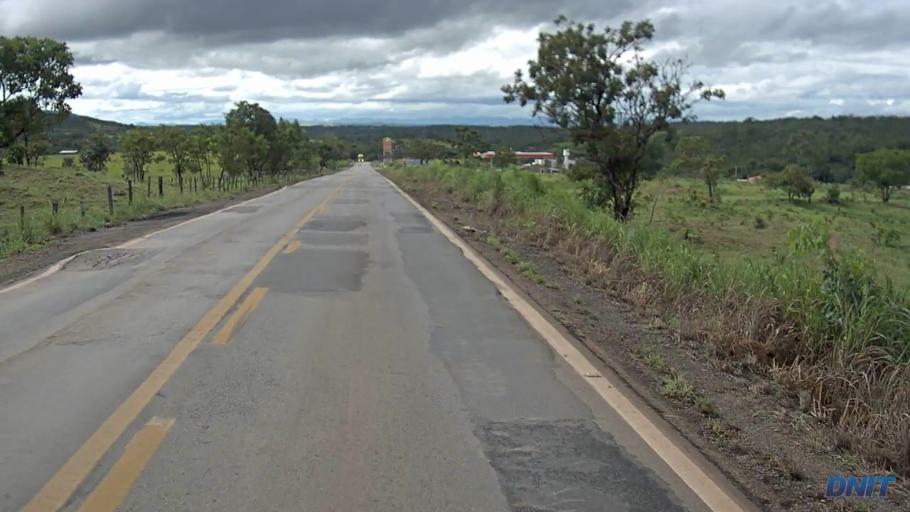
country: BR
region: Goias
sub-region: Padre Bernardo
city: Padre Bernardo
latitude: -15.4306
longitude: -48.1940
